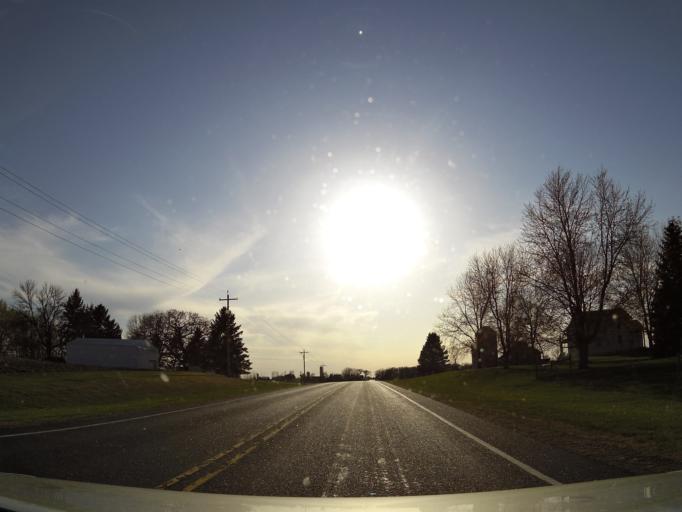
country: US
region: Wisconsin
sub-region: Pierce County
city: River Falls
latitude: 44.8244
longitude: -92.7107
